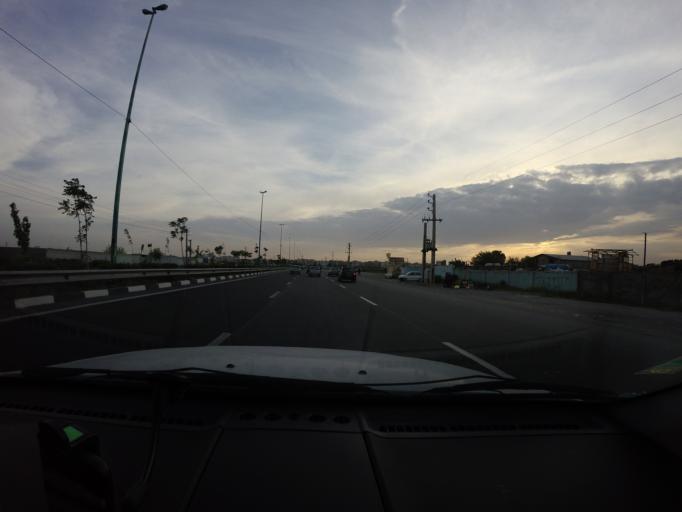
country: IR
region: Tehran
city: Eslamshahr
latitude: 35.5353
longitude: 51.2380
